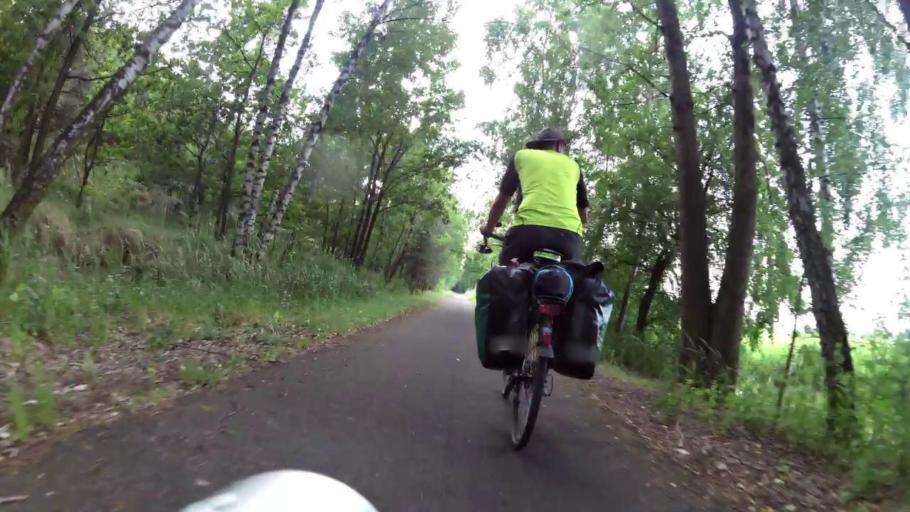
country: PL
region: Kujawsko-Pomorskie
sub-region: Powiat chelminski
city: Unislaw
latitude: 53.1863
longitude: 18.3786
